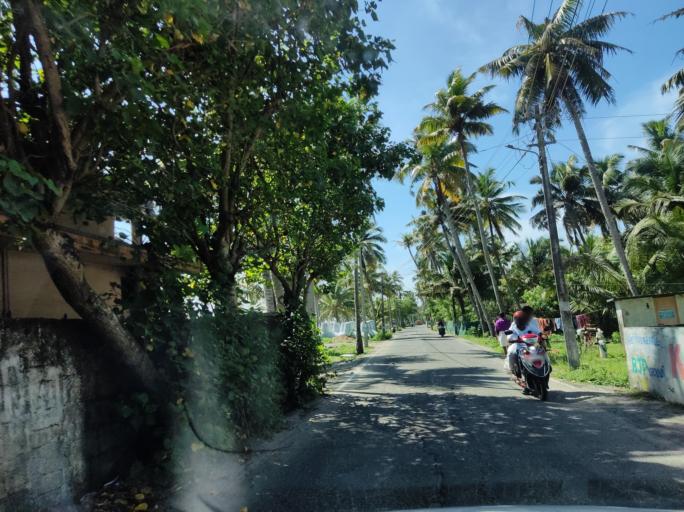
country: IN
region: Kerala
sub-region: Alappuzha
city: Kayankulam
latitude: 9.2406
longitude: 76.4157
